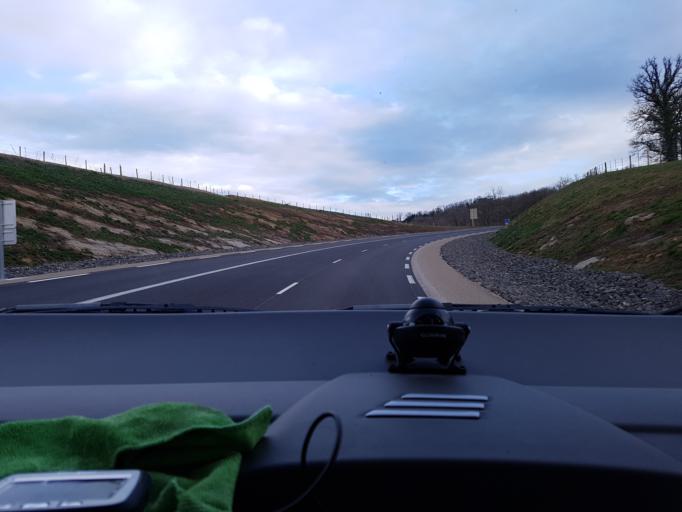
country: FR
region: Midi-Pyrenees
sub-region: Departement de l'Aveyron
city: Espalion
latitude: 44.5227
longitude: 2.7337
